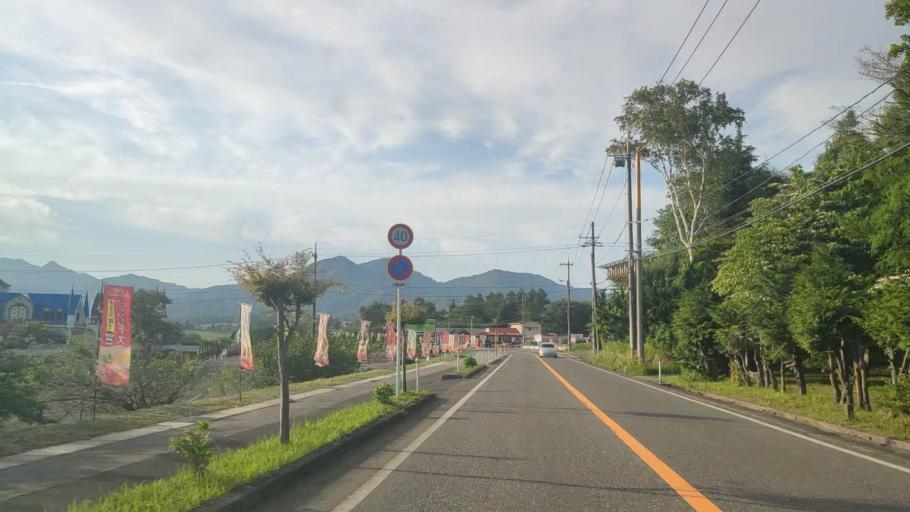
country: JP
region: Tottori
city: Kurayoshi
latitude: 35.2899
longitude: 133.6366
